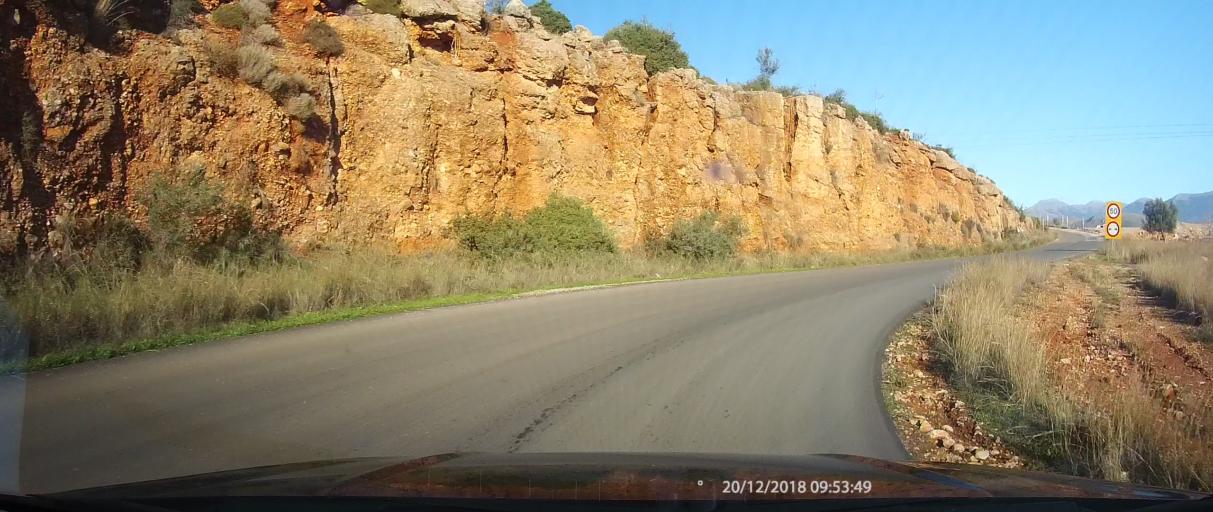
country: GR
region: Peloponnese
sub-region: Nomos Lakonias
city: Yerakion
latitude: 37.0106
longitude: 22.6372
